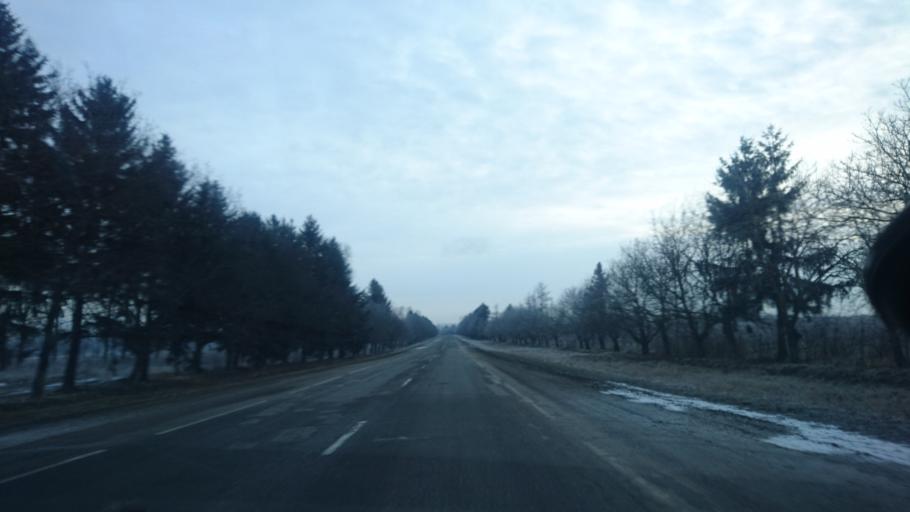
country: MD
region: Briceni
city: Briceni
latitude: 48.3035
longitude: 27.1242
